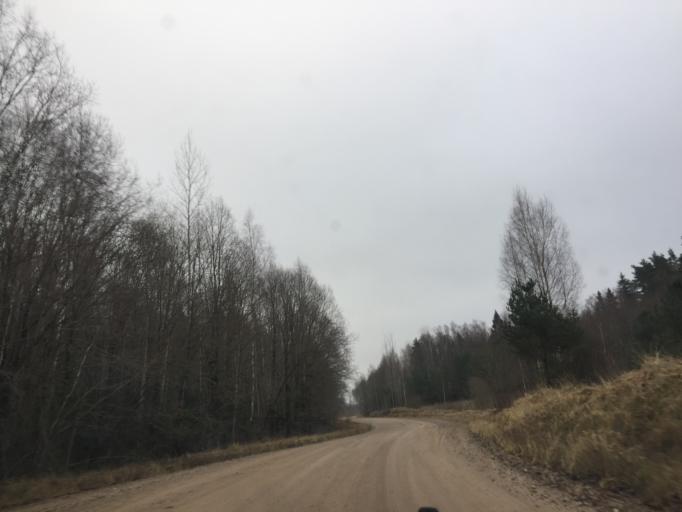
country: LV
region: Limbazu Rajons
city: Limbazi
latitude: 57.5929
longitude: 24.6292
